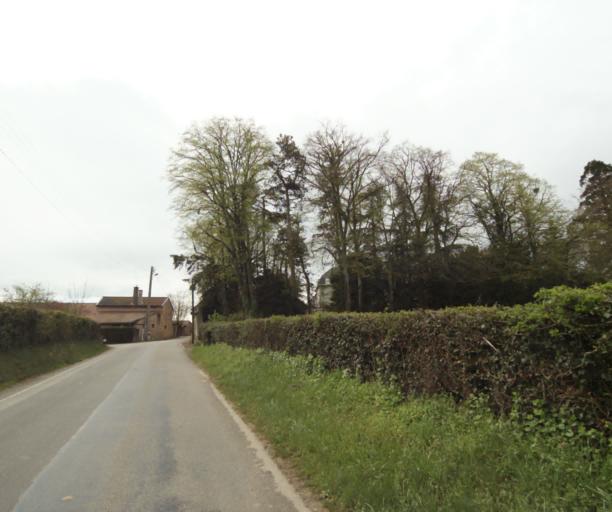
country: FR
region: Bourgogne
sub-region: Departement de Saone-et-Loire
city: Charnay-les-Macon
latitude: 46.3112
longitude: 4.7854
